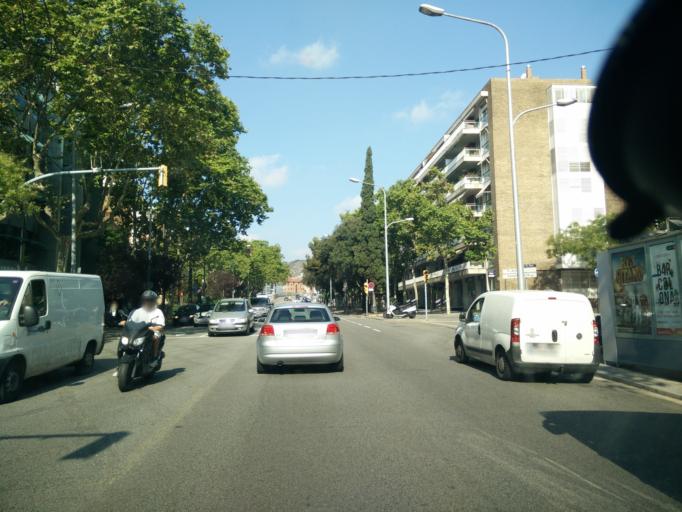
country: ES
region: Catalonia
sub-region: Provincia de Barcelona
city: Sarria-Sant Gervasi
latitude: 41.3978
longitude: 2.1304
